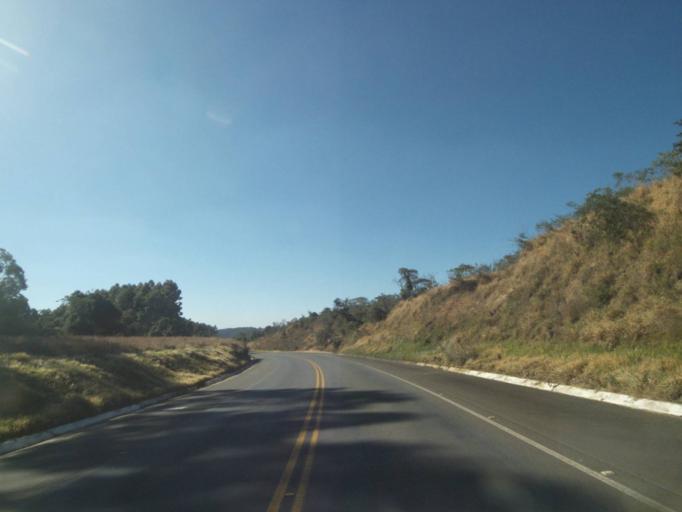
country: BR
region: Parana
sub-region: Tibagi
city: Tibagi
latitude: -24.7537
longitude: -50.4666
